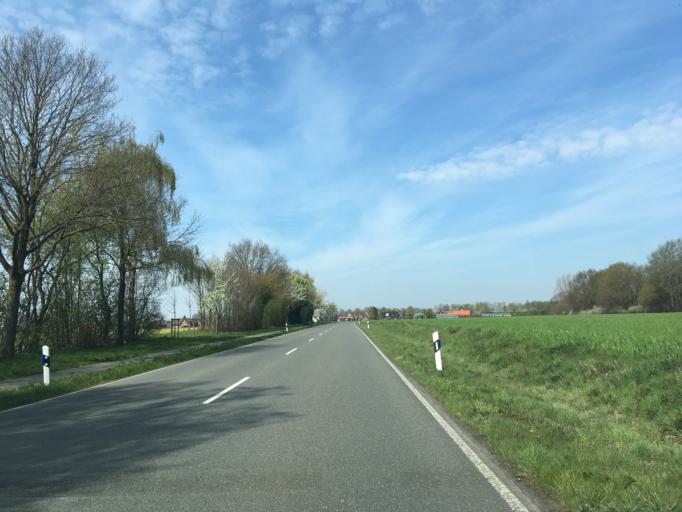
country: DE
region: North Rhine-Westphalia
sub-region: Regierungsbezirk Munster
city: Vreden
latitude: 52.0209
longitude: 6.8389
